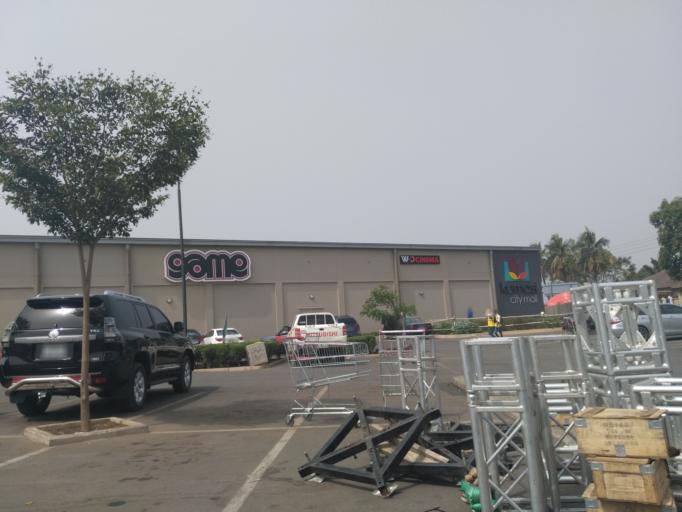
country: GH
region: Ashanti
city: Kumasi
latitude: 6.6738
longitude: -1.6071
